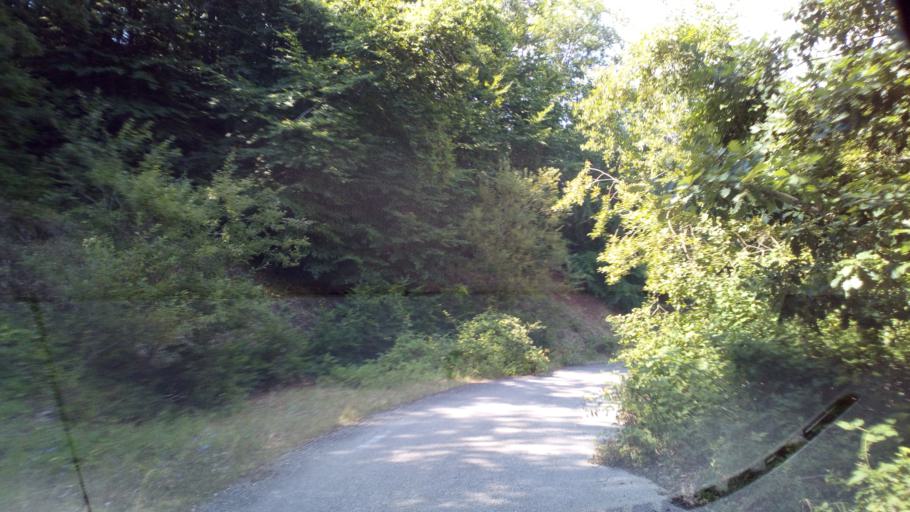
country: GR
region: Central Macedonia
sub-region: Nomos Thessalonikis
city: Sochos
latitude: 40.8309
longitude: 23.3533
